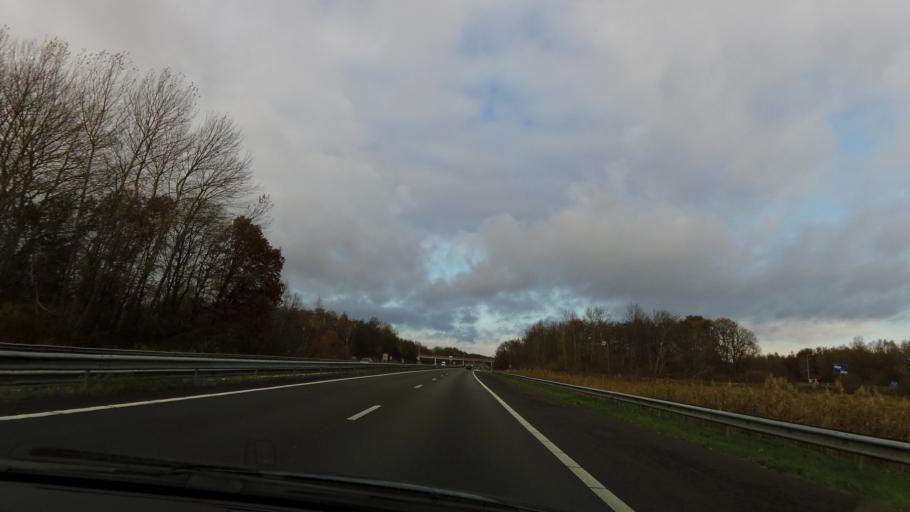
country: NL
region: Limburg
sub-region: Gemeente Venray
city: Venray
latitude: 51.5179
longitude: 6.0046
